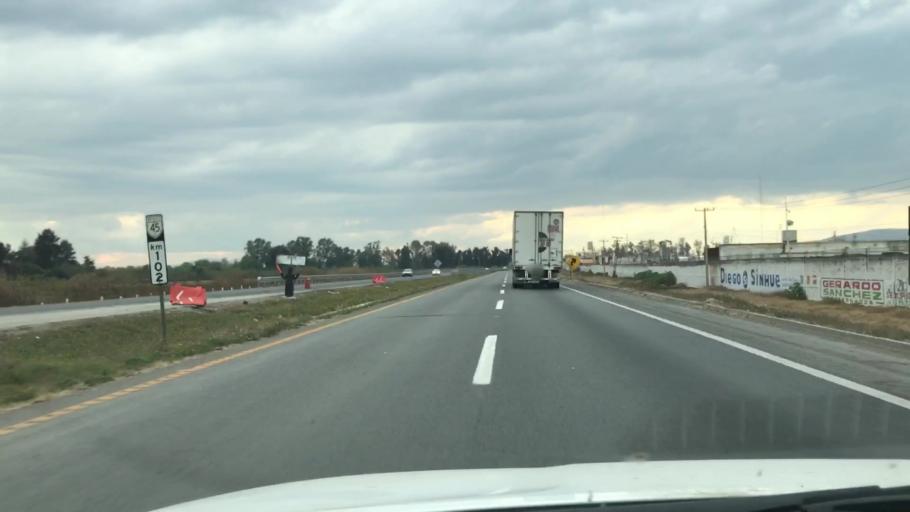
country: MX
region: Guanajuato
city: Irapuato
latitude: 20.6496
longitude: -101.3476
